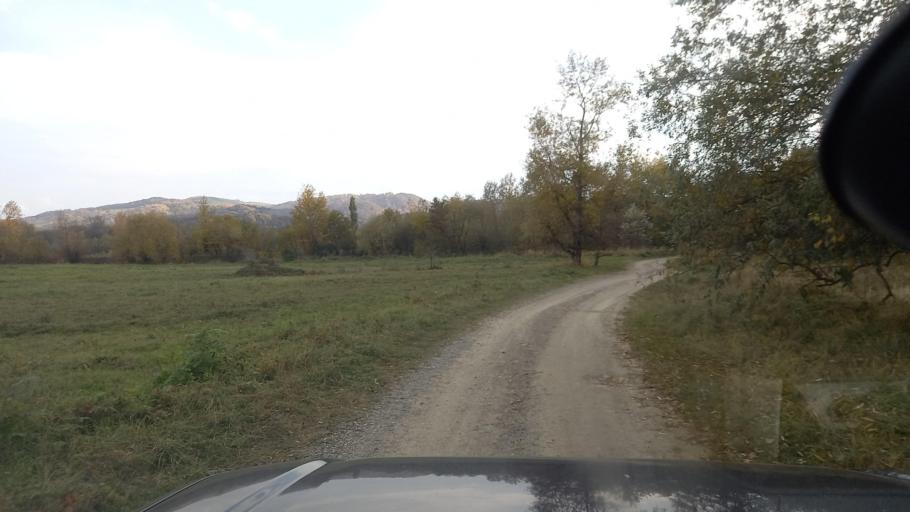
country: RU
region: Krasnodarskiy
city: Shedok
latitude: 44.1780
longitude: 40.8504
